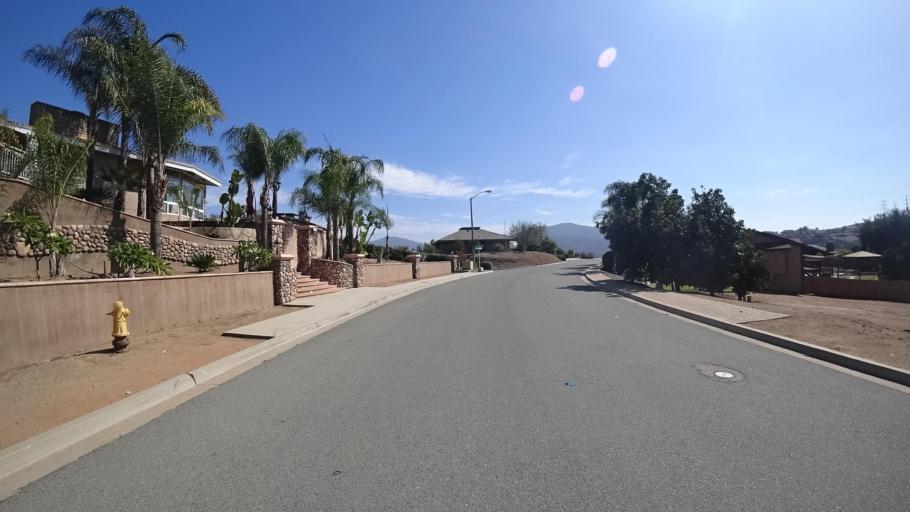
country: US
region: California
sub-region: San Diego County
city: Granite Hills
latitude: 32.7869
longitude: -116.8925
